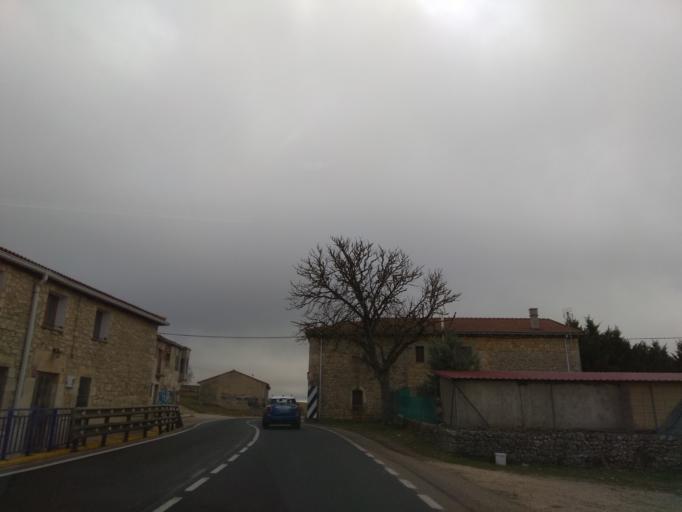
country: ES
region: Castille and Leon
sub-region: Provincia de Burgos
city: Tubilla del Agua
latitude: 42.6465
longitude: -3.8842
